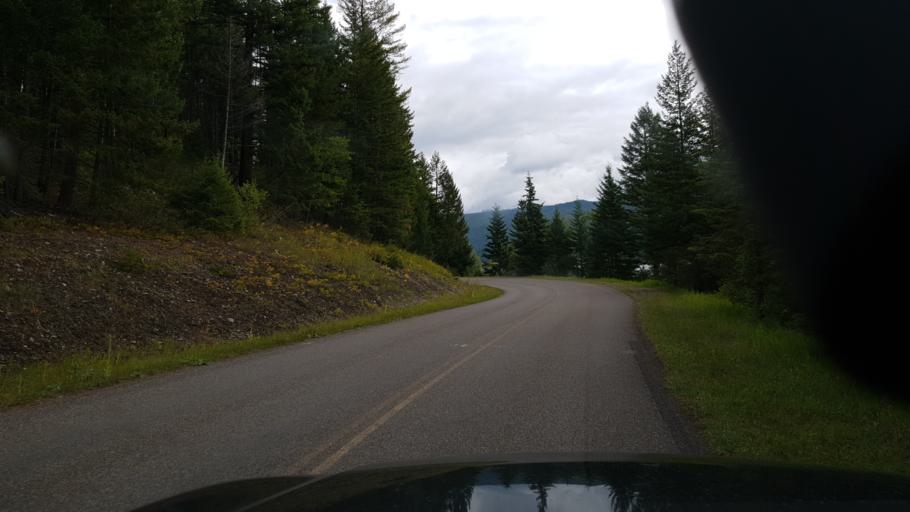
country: US
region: Montana
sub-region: Flathead County
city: Columbia Falls
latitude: 48.5440
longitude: -113.9898
